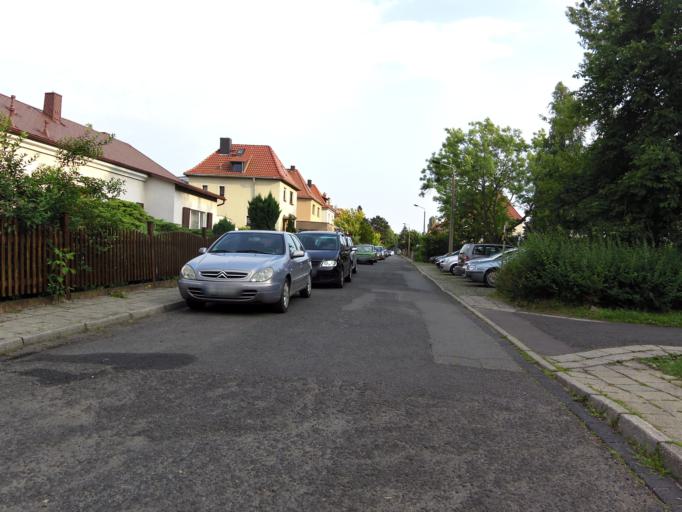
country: DE
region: Saxony
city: Markkleeberg
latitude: 51.3053
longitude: 12.3195
